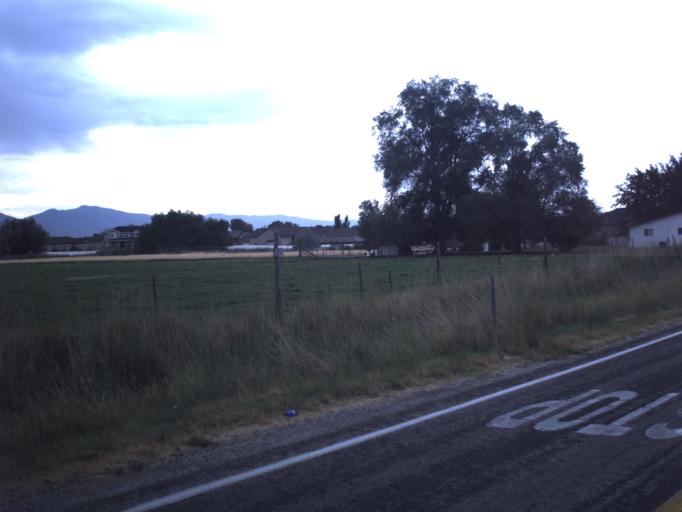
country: US
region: Utah
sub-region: Weber County
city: Hooper
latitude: 41.1379
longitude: -112.1126
